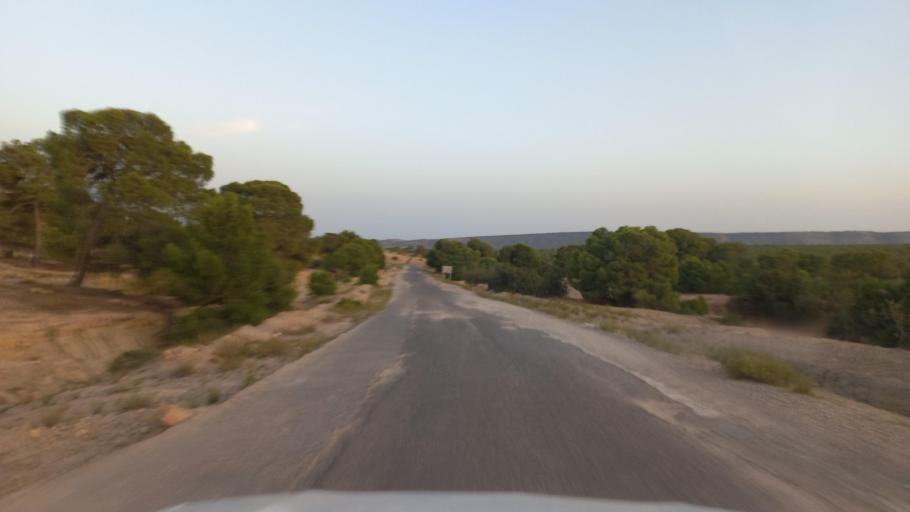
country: TN
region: Al Qasrayn
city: Sbiba
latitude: 35.4163
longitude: 8.9257
